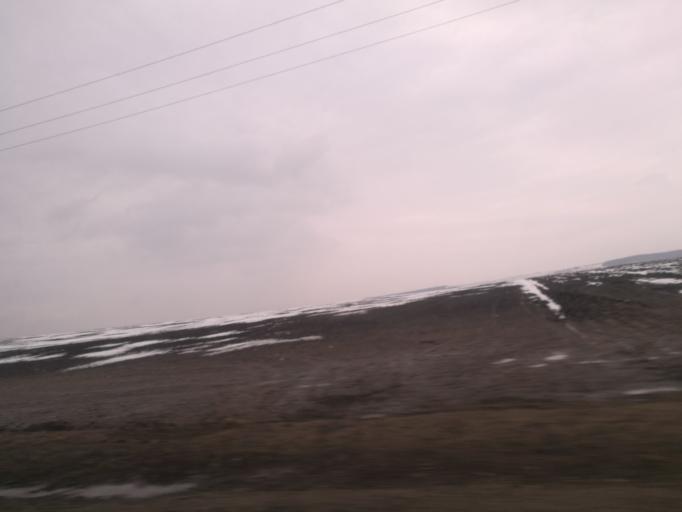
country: RO
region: Iasi
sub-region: Comuna Targu Frumos
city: Targu Frumos
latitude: 47.2058
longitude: 26.9825
